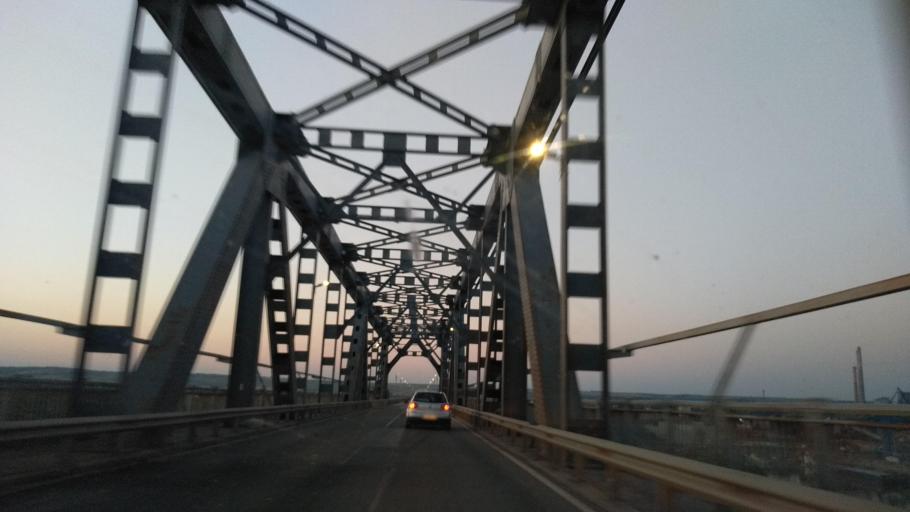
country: RO
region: Giurgiu
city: Giurgiu
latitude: 43.8865
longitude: 26.0083
